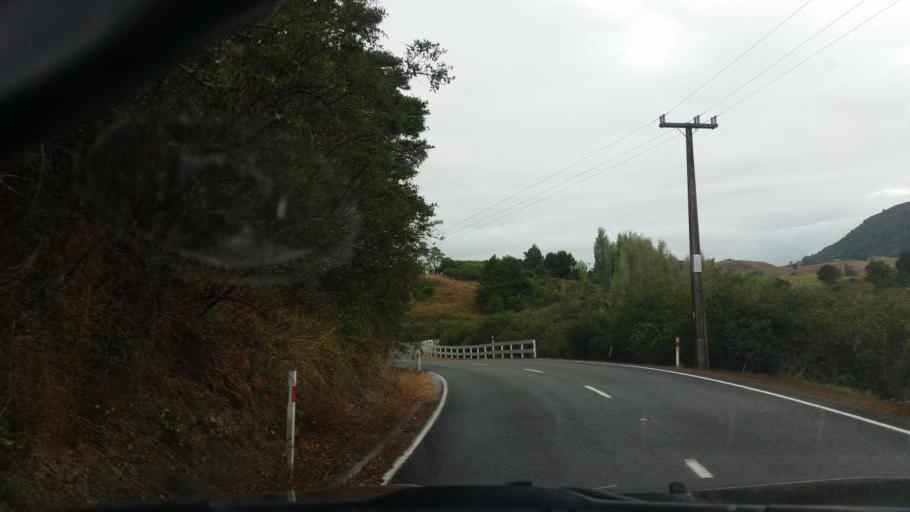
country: NZ
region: Auckland
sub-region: Auckland
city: Wellsford
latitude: -36.1208
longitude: 174.3633
